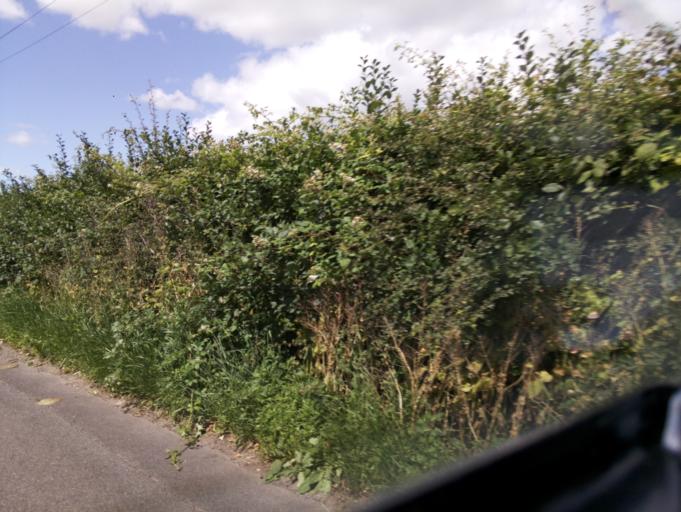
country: GB
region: England
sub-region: Nottinghamshire
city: Burton Joyce
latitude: 53.0043
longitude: -1.0763
